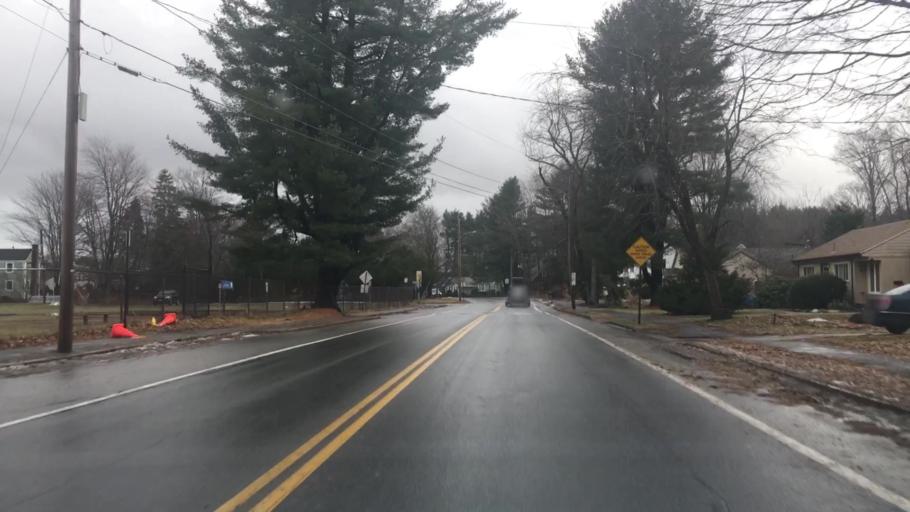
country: US
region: Maine
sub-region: Cumberland County
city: South Portland Gardens
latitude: 43.6721
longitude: -70.3142
